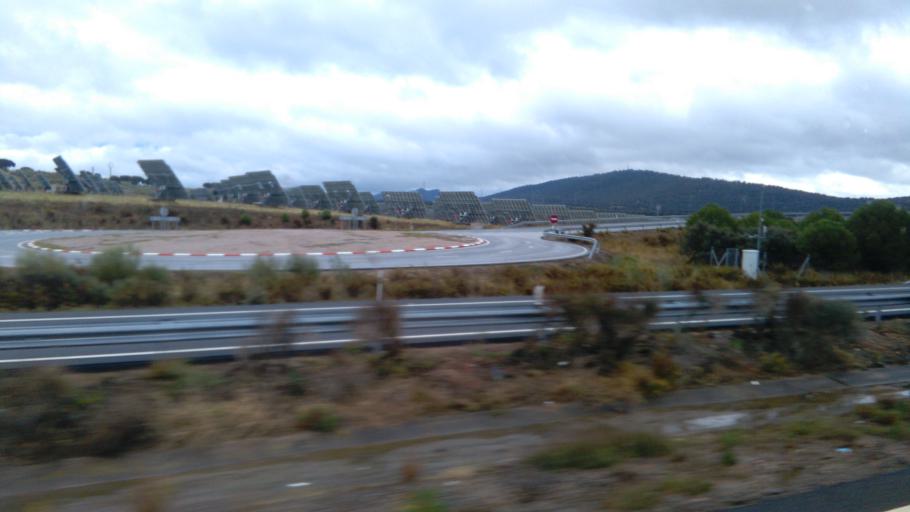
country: ES
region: Extremadura
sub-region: Provincia de Caceres
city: Almaraz
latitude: 39.8294
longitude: -5.6573
